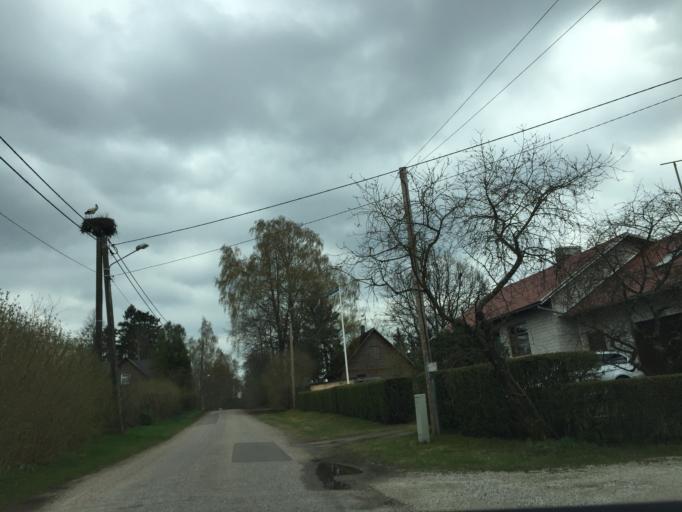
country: EE
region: Tartu
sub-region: Noo vald
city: Noo
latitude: 58.2704
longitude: 26.5369
